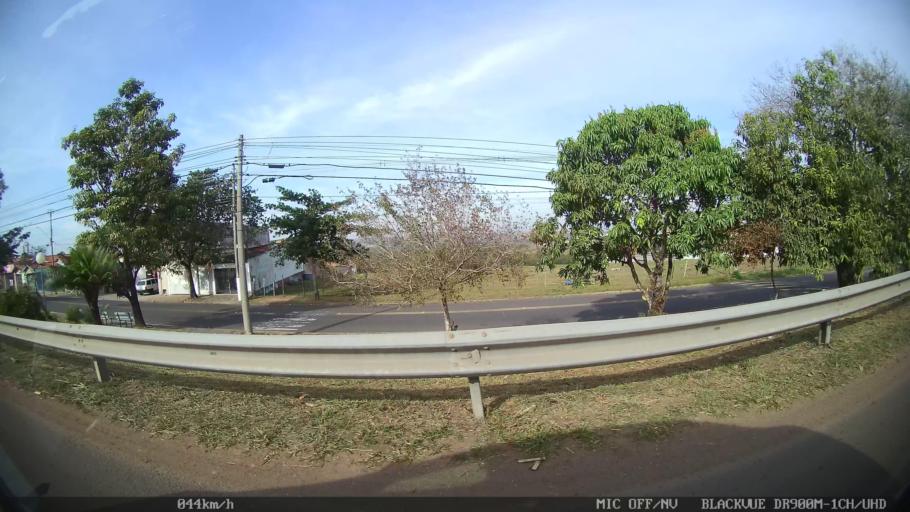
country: BR
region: Sao Paulo
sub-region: Piracicaba
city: Piracicaba
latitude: -22.6800
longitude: -47.7050
